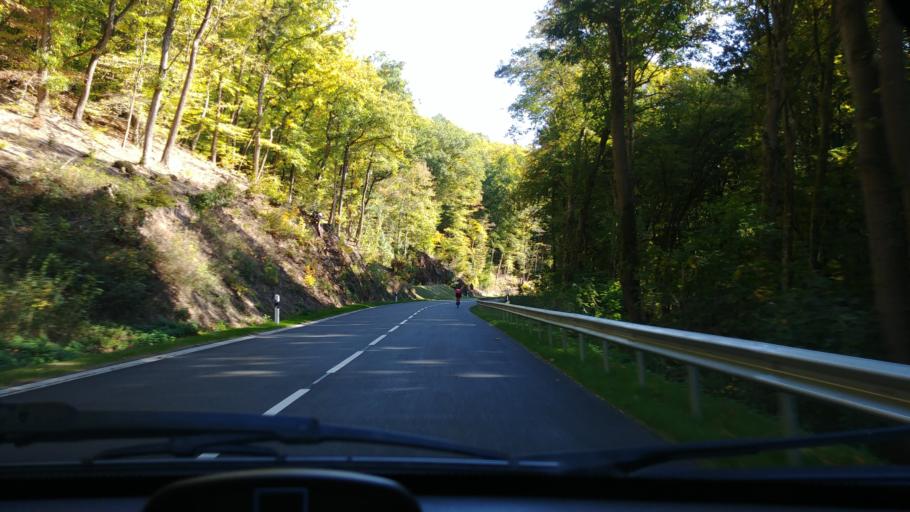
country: DE
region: Rheinland-Pfalz
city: Mudershausen
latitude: 50.2869
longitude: 8.0458
